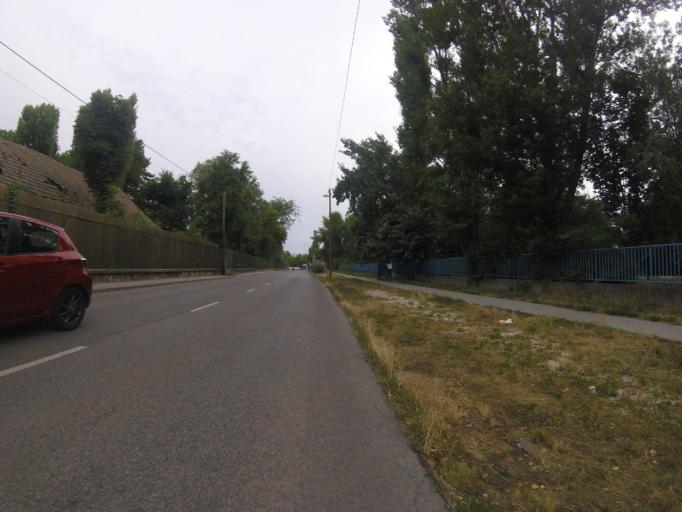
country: HU
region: Pest
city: Budakalasz
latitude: 47.5956
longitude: 19.0672
